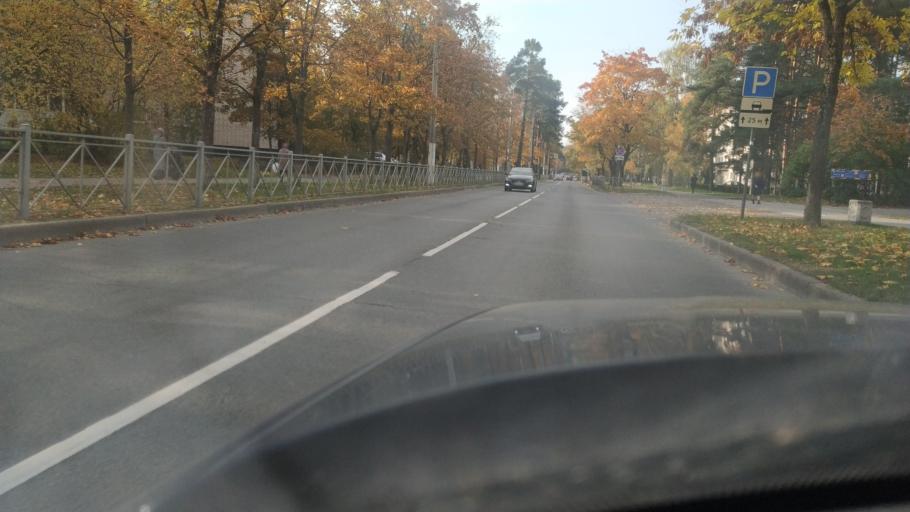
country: RU
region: Leningrad
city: Sosnovyy Bor
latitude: 59.8916
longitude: 29.0934
